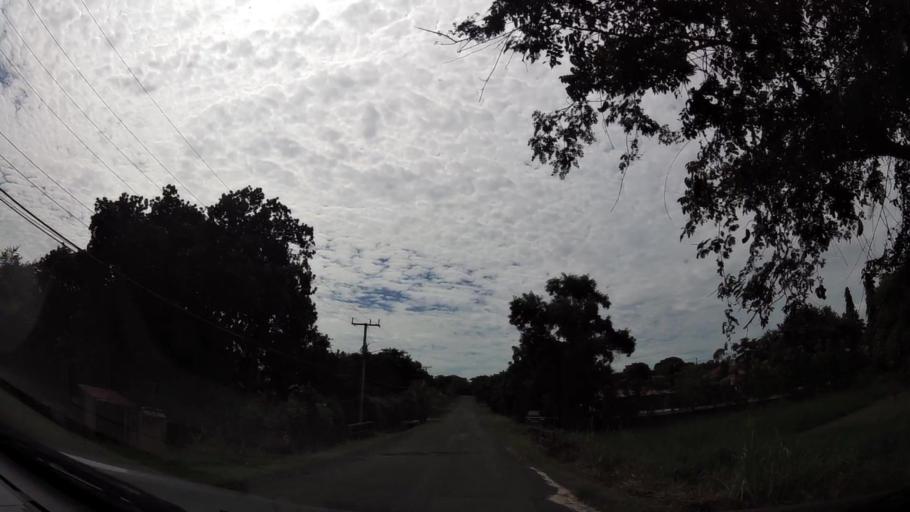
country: PA
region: Panama
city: Nueva Gorgona
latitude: 8.5385
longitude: -79.8988
